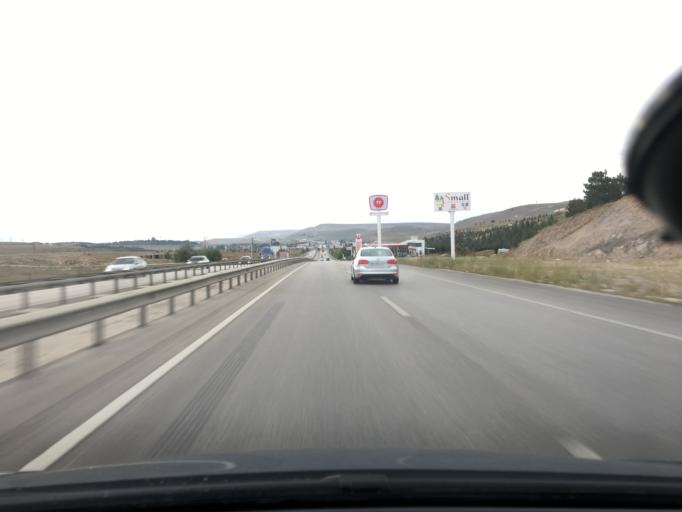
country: TR
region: Afyonkarahisar
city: Afyonkarahisar
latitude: 38.7923
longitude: 30.4146
